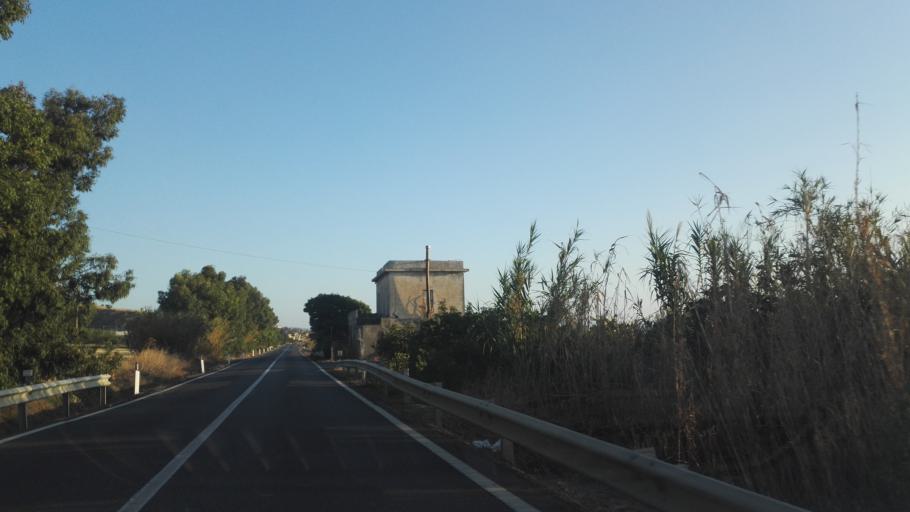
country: IT
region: Calabria
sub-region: Provincia di Catanzaro
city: Santa Caterina dello Ionio Marina
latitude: 38.5074
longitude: 16.5753
